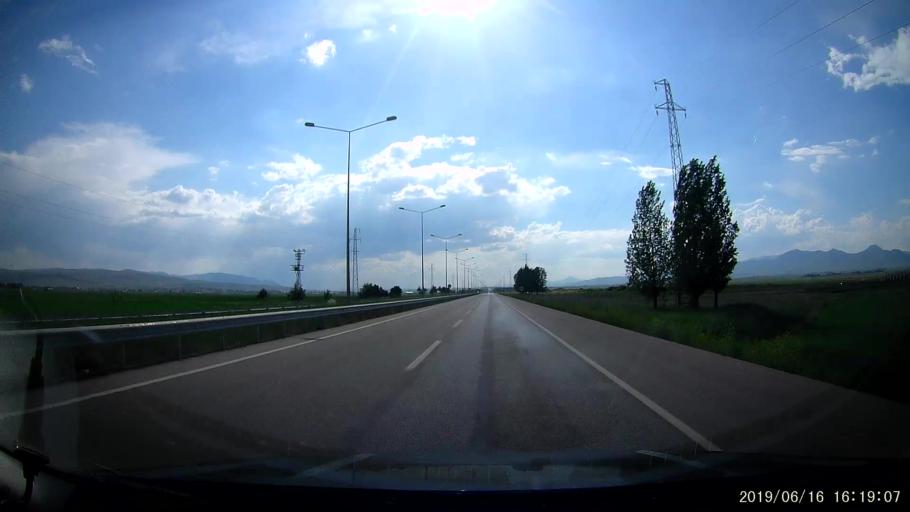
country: TR
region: Erzurum
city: Ilica
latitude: 39.9660
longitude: 41.1489
